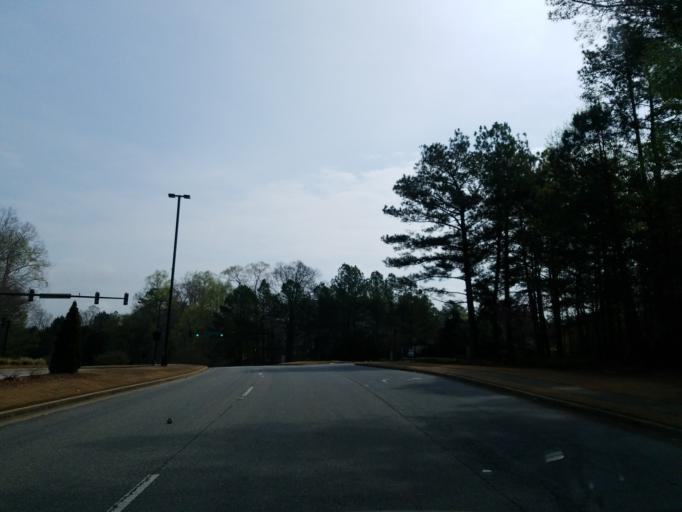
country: US
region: Georgia
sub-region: Fulton County
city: Johns Creek
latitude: 34.0894
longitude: -84.2275
